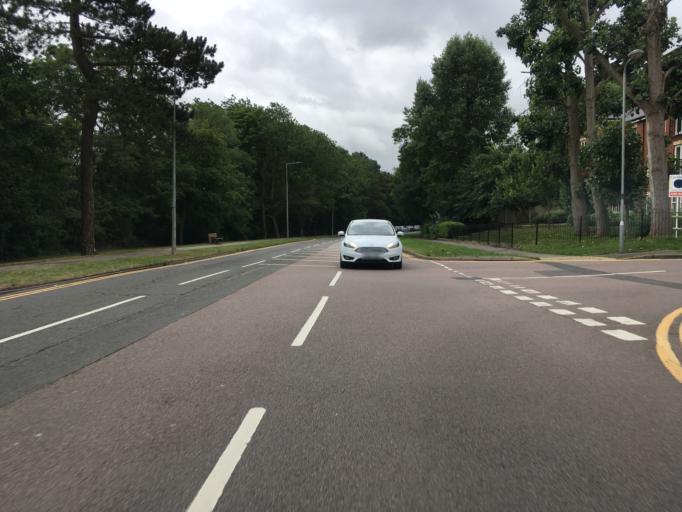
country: GB
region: England
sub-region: Buckinghamshire
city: Bletchley
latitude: 51.9997
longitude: -0.7385
